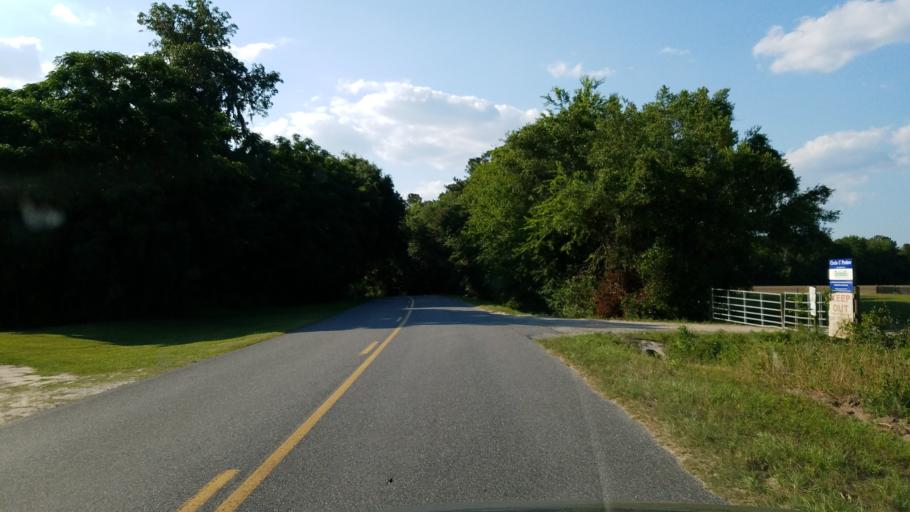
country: US
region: Georgia
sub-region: Echols County
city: Statenville
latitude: 30.6188
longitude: -83.0968
